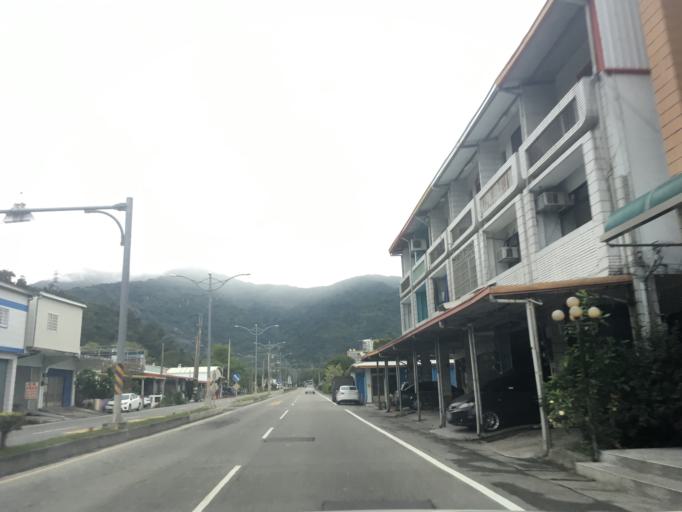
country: TW
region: Taiwan
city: Taitung City
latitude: 22.6953
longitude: 121.0451
